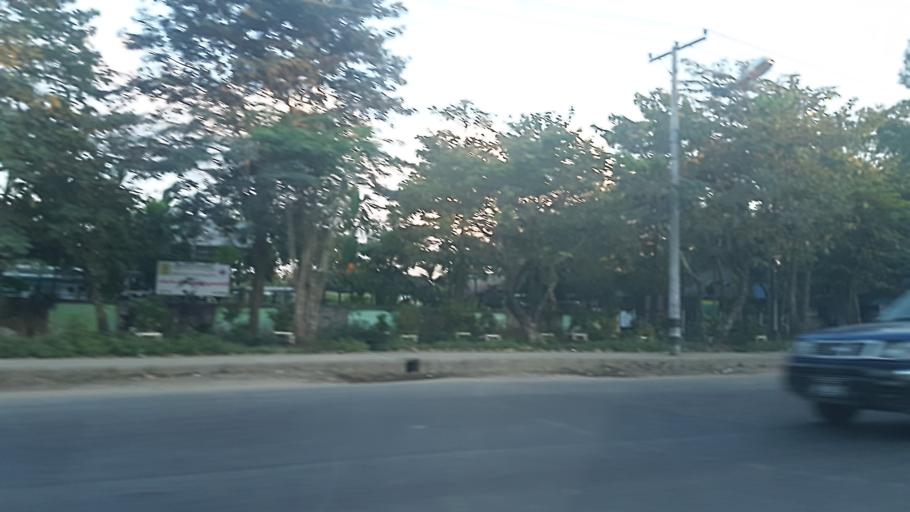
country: MM
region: Yangon
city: Yangon
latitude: 16.8961
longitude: 96.1220
